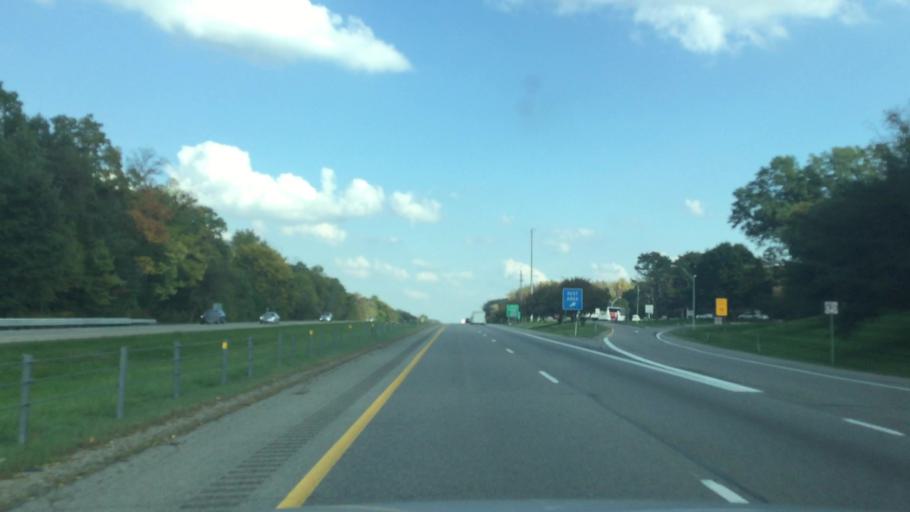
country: US
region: Michigan
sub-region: Calhoun County
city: Lakeview
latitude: 42.2646
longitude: -85.2228
